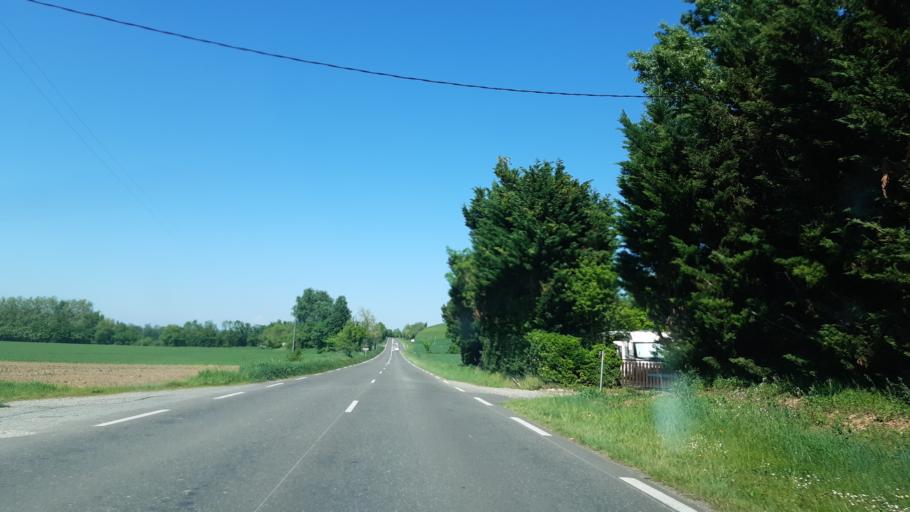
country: FR
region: Midi-Pyrenees
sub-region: Departement du Gers
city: Pujaudran
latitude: 43.5868
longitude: 1.0509
